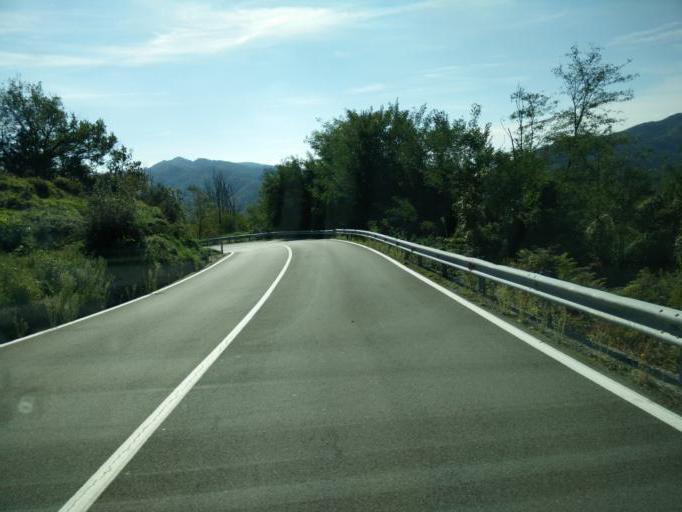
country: IT
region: Liguria
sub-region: Provincia di La Spezia
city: Carrodano
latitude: 44.2448
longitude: 9.6318
